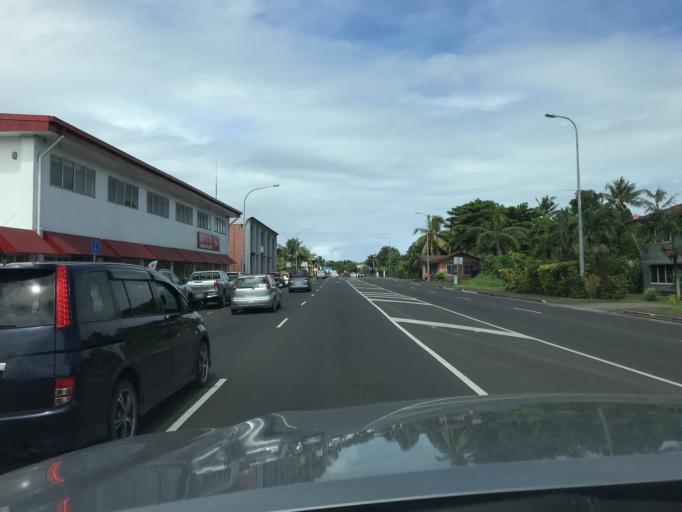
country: WS
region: Tuamasaga
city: Apia
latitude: -13.8385
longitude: -171.7751
